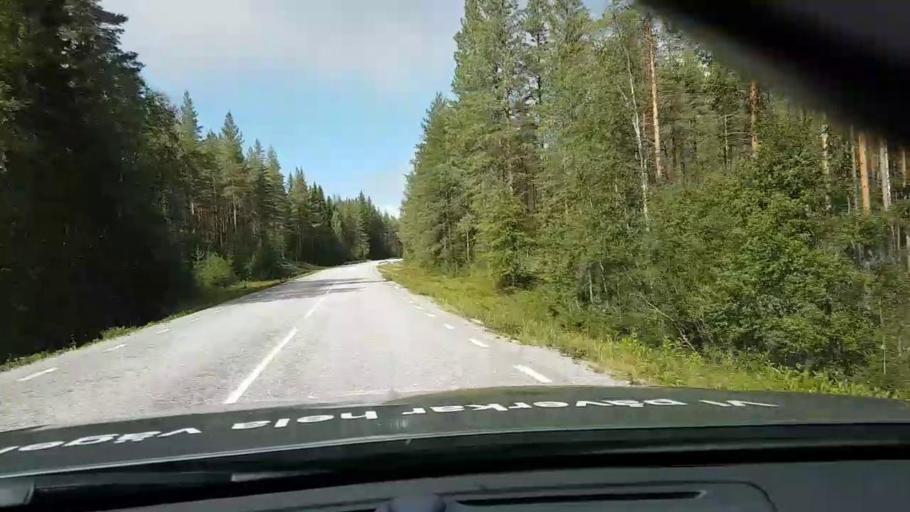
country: SE
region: Vaesternorrland
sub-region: OErnskoeldsviks Kommun
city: Bredbyn
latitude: 63.6936
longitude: 17.7668
